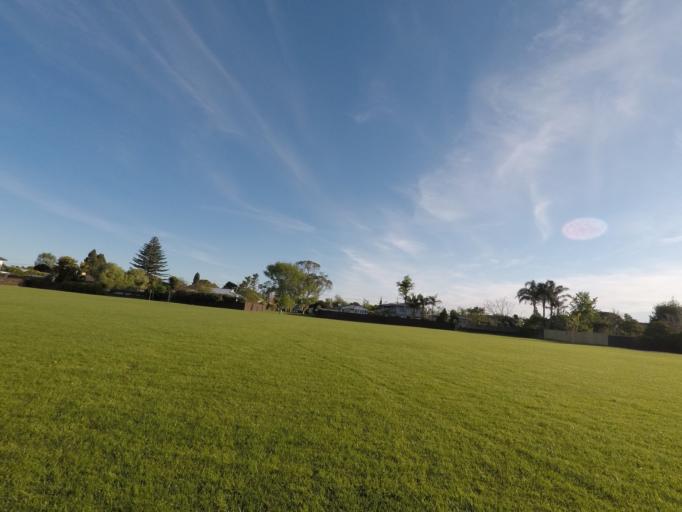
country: NZ
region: Auckland
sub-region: Auckland
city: Rosebank
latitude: -36.8429
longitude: 174.6488
